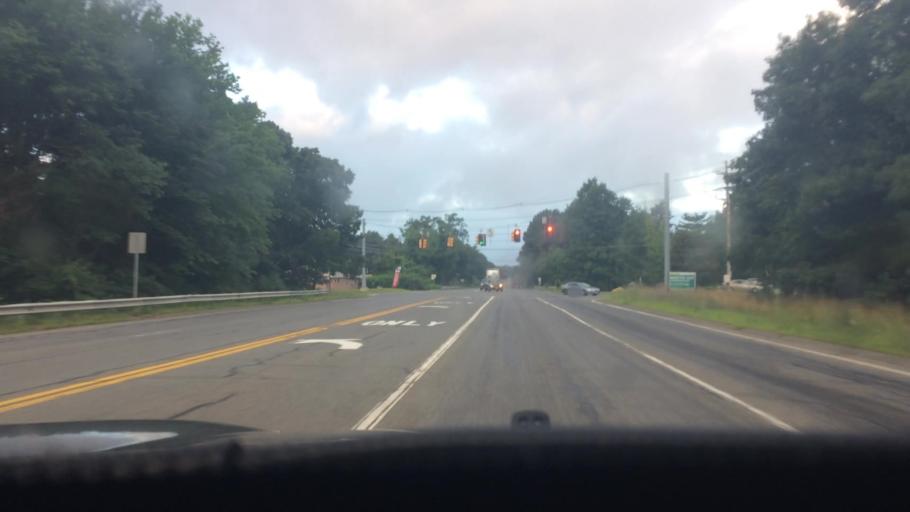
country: US
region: Massachusetts
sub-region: Middlesex County
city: Wilmington
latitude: 42.5923
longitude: -71.1466
